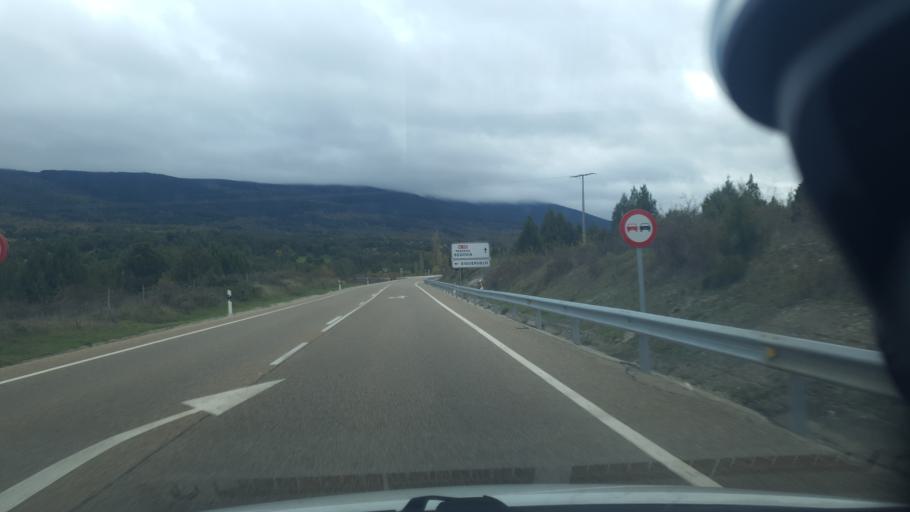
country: ES
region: Castille and Leon
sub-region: Provincia de Segovia
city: Casla
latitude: 41.1750
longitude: -3.6407
